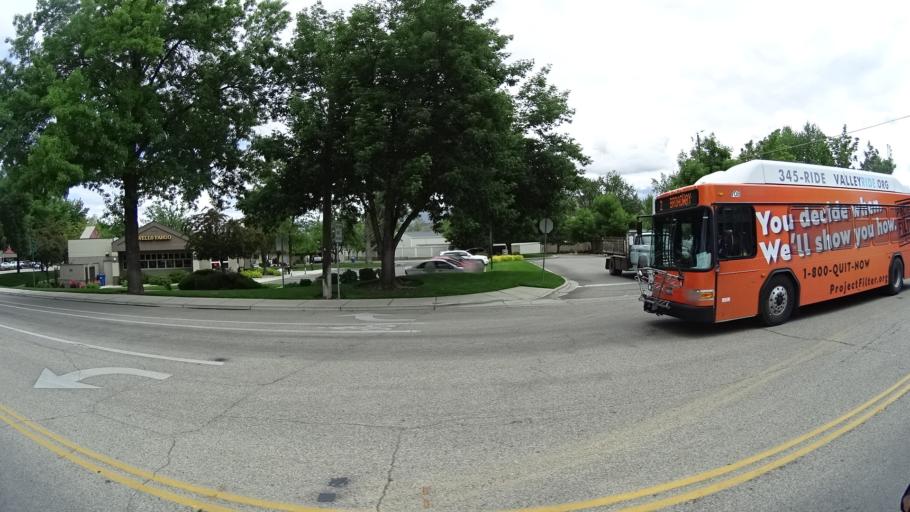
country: US
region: Idaho
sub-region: Ada County
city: Boise
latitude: 43.5782
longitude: -116.1730
